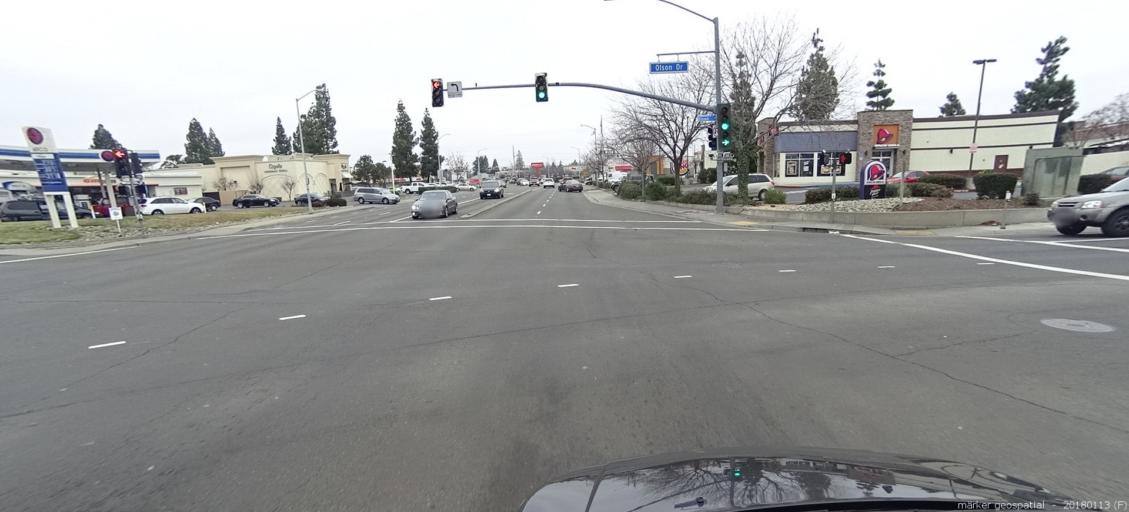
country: US
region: California
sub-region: Sacramento County
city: Rancho Cordova
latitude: 38.5936
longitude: -121.2878
